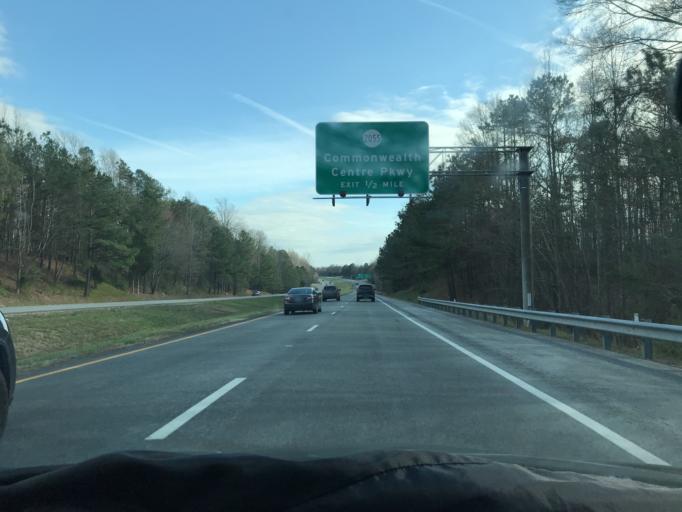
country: US
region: Virginia
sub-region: Chesterfield County
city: Brandermill
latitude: 37.4320
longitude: -77.6337
